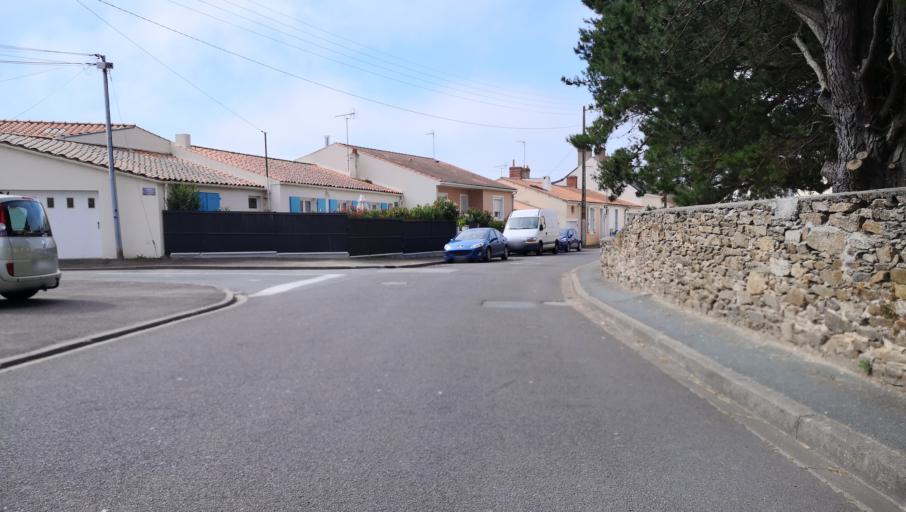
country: FR
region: Pays de la Loire
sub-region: Departement de la Vendee
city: Les Sables-d'Olonne
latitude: 46.5031
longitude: -1.7829
